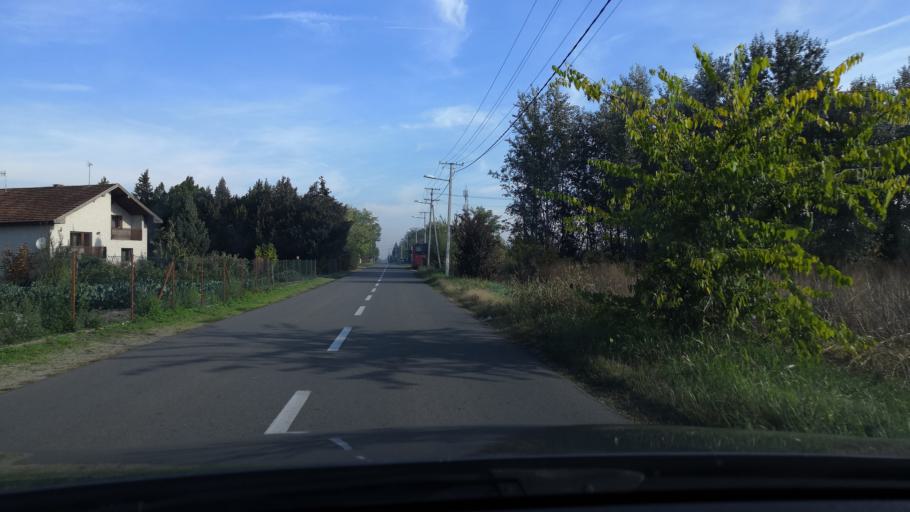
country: HU
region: Csongrad
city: Asotthalom
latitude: 46.1157
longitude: 19.8417
